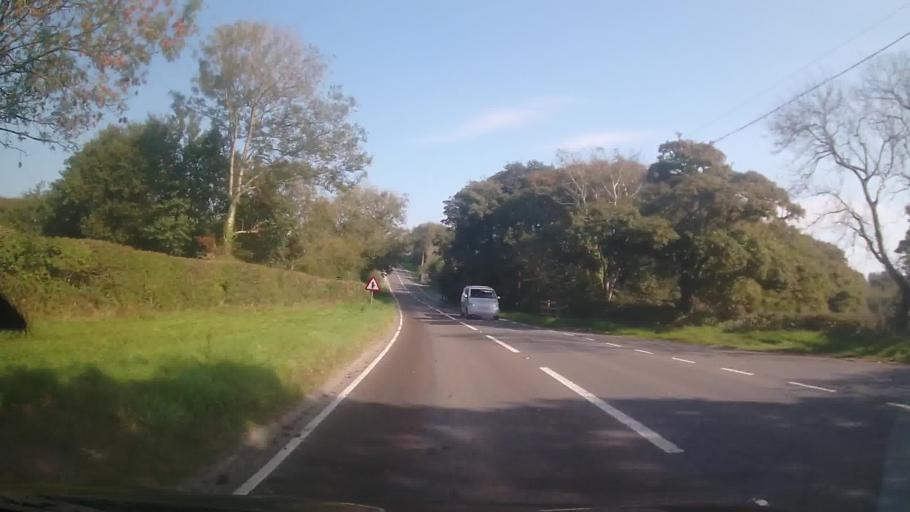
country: GB
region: Wales
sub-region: Pembrokeshire
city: Nevern
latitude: 52.0094
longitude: -4.7366
